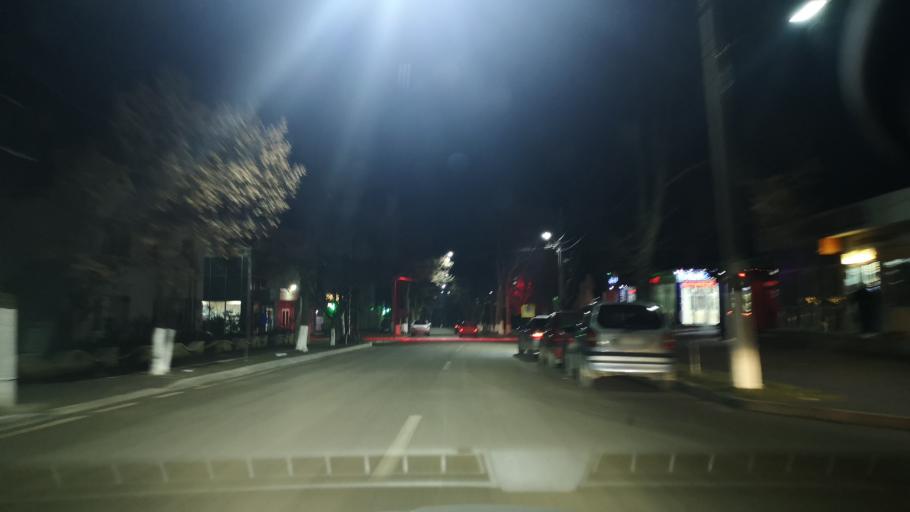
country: MD
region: Orhei
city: Orhei
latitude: 47.3869
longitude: 28.8246
